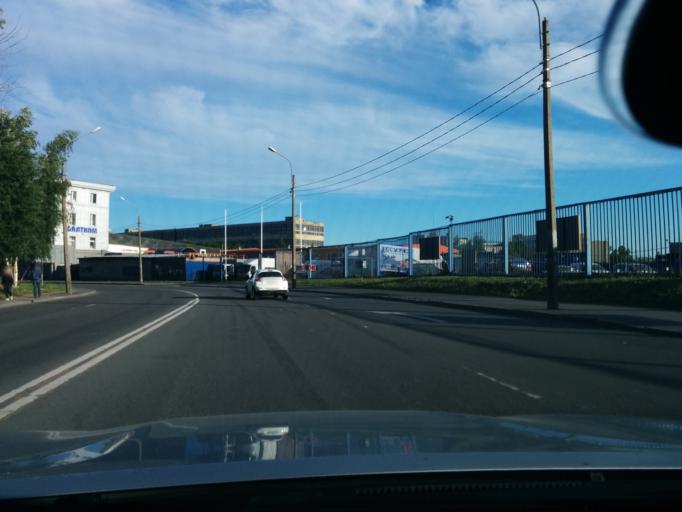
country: RU
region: Leningrad
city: Finlyandskiy
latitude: 59.9773
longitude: 30.3677
